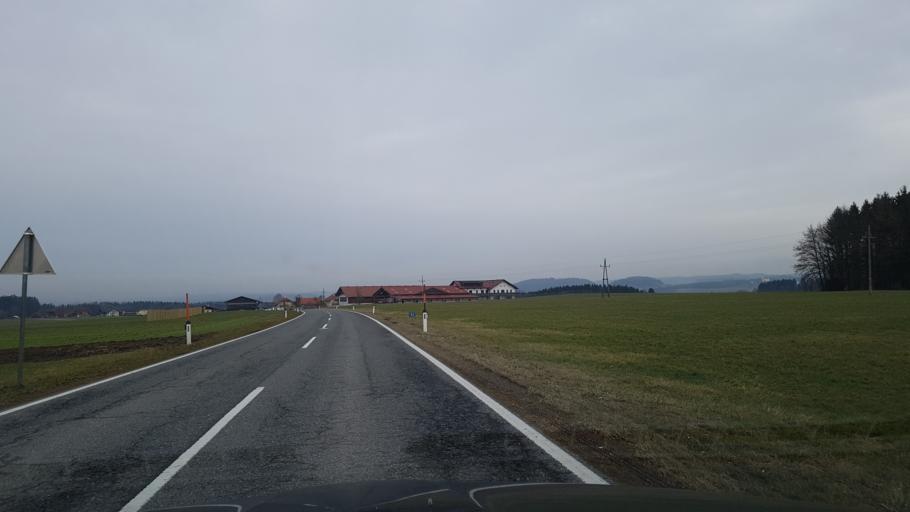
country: AT
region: Salzburg
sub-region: Politischer Bezirk Salzburg-Umgebung
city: Lamprechtshausen
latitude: 48.0217
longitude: 12.9588
